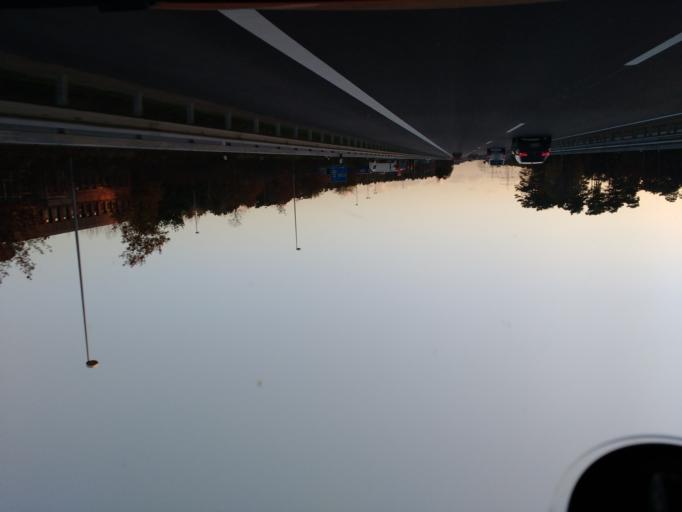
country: DE
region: Schleswig-Holstein
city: Gudow
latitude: 53.5194
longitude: 10.8108
